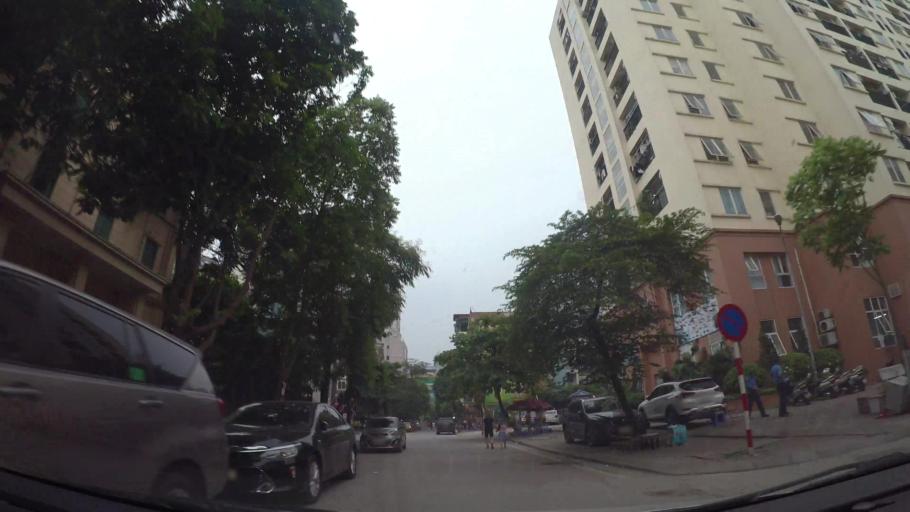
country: VN
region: Ha Noi
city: Cau Dien
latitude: 21.0374
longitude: 105.7656
